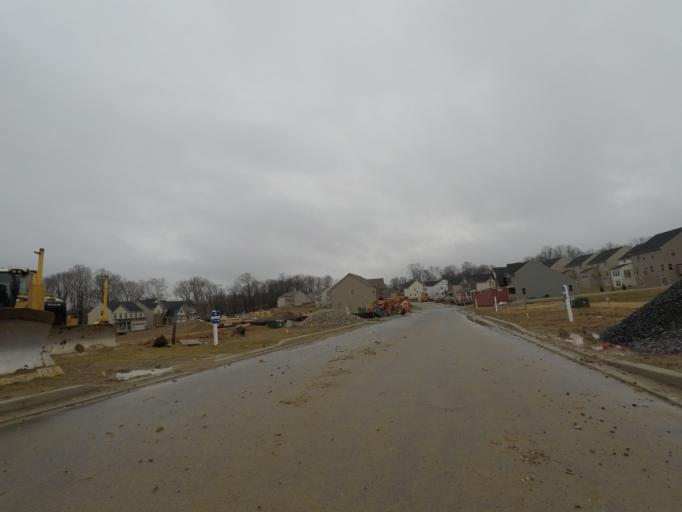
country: US
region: Maryland
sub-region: Howard County
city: Ellicott City
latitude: 39.3067
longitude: -76.8195
